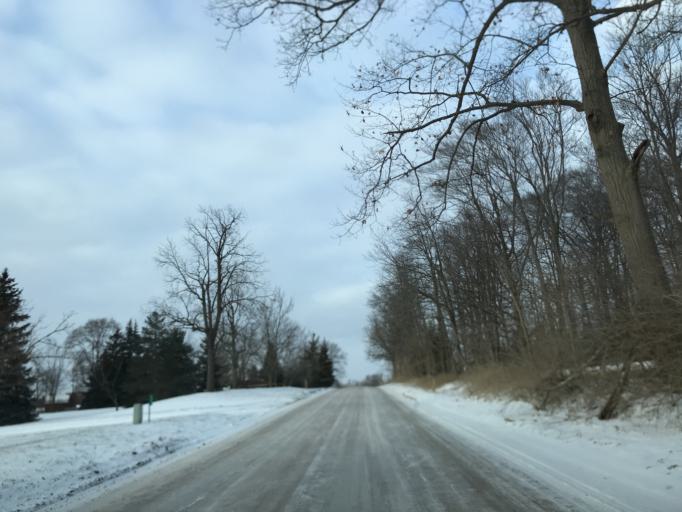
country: US
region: Michigan
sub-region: Oakland County
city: South Lyon
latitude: 42.4580
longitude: -83.5925
